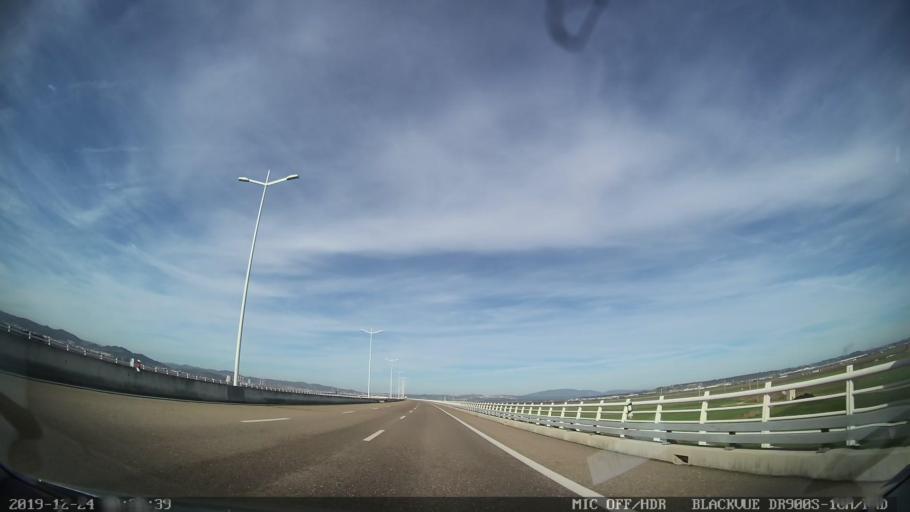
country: PT
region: Lisbon
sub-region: Vila Franca de Xira
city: Castanheira do Ribatejo
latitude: 39.0047
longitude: -8.9087
